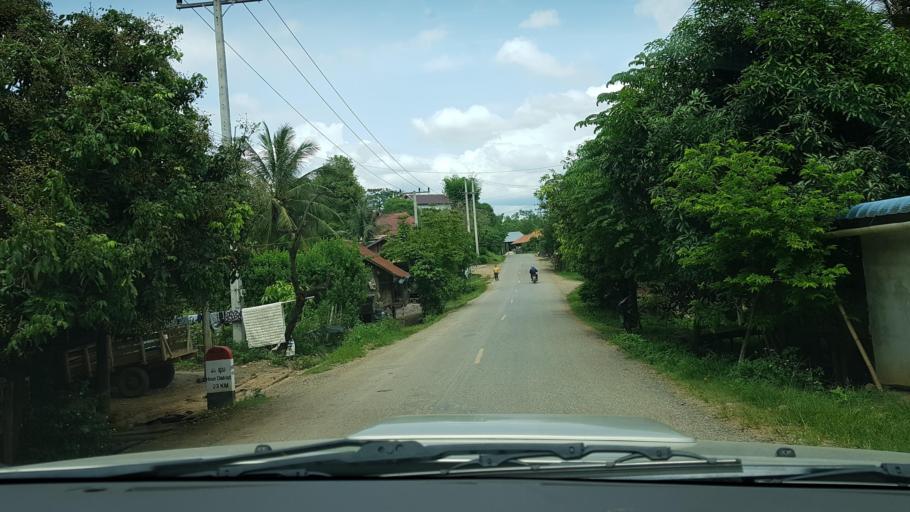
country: TH
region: Nan
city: Chaloem Phra Kiat
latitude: 20.0113
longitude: 101.3123
